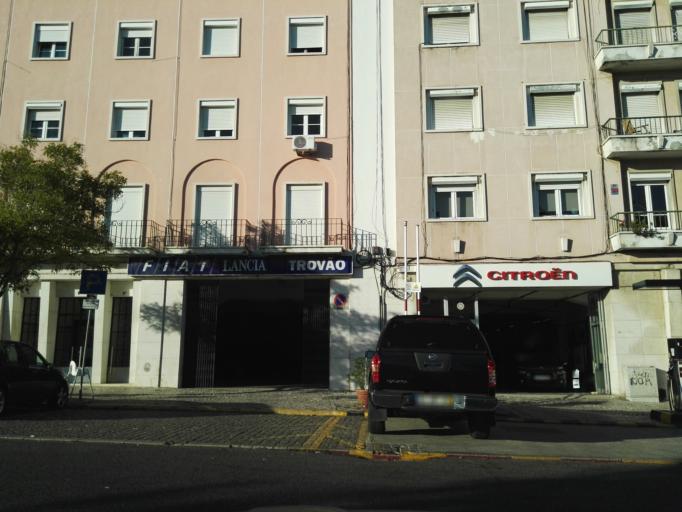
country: PT
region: Lisbon
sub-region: Lisbon
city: Lisbon
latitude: 38.7415
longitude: -9.1389
